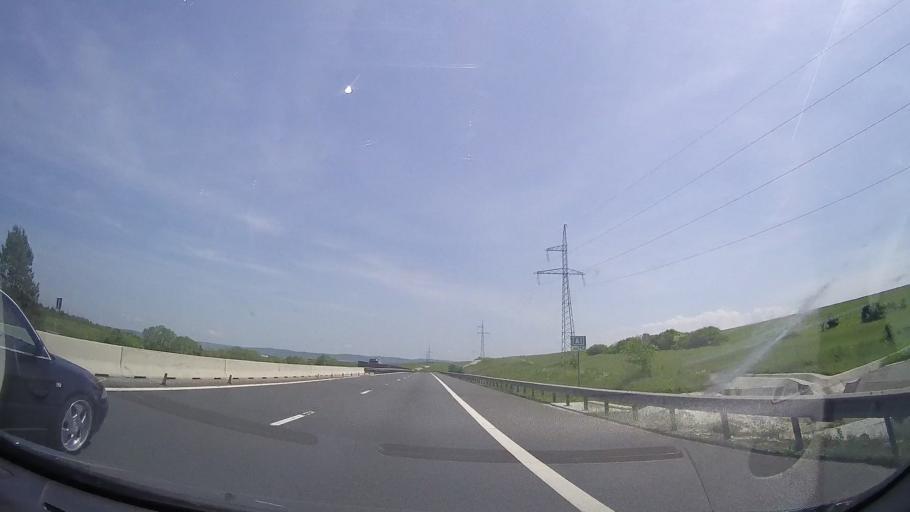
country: RO
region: Sibiu
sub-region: Comuna Cristian
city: Cristian
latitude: 45.8019
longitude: 24.0447
